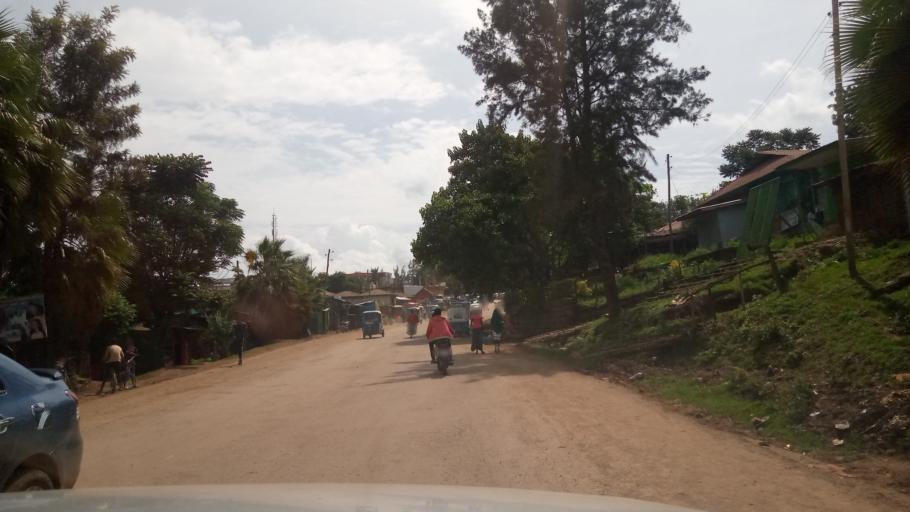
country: ET
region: Oromiya
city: Agaro
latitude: 7.8553
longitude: 36.5891
